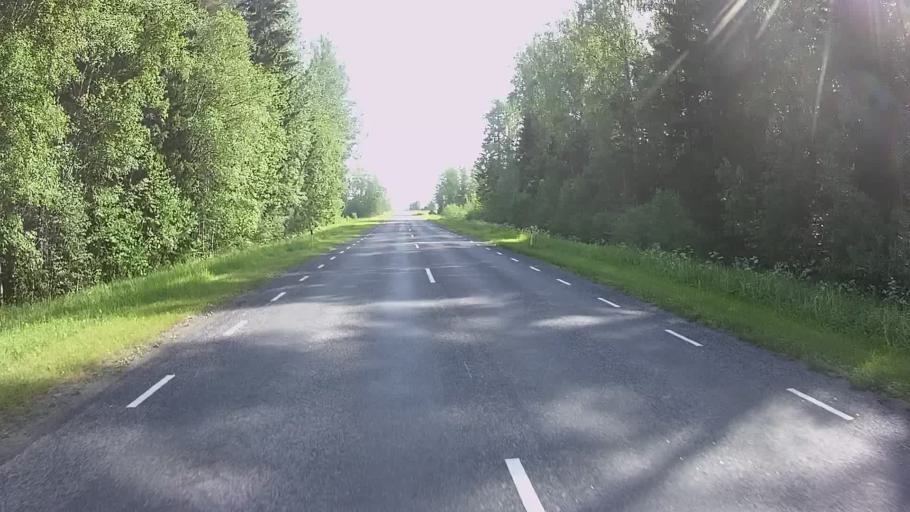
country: EE
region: Valgamaa
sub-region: Torva linn
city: Torva
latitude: 58.0618
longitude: 26.0203
